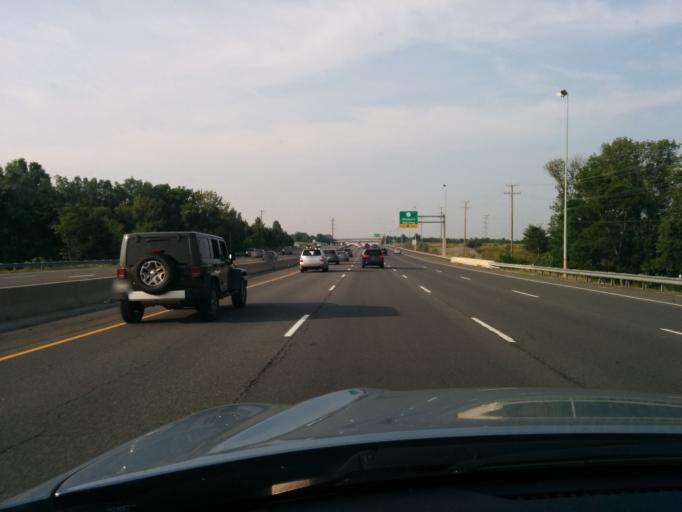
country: US
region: Virginia
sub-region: Loudoun County
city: Sterling
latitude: 39.0179
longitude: -77.4322
